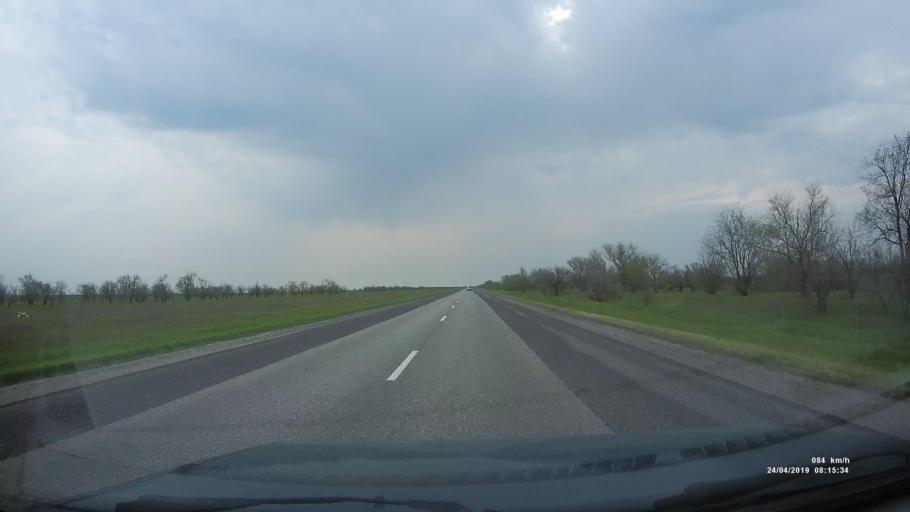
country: RU
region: Kalmykiya
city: Priyutnoye
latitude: 46.1000
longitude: 43.5969
